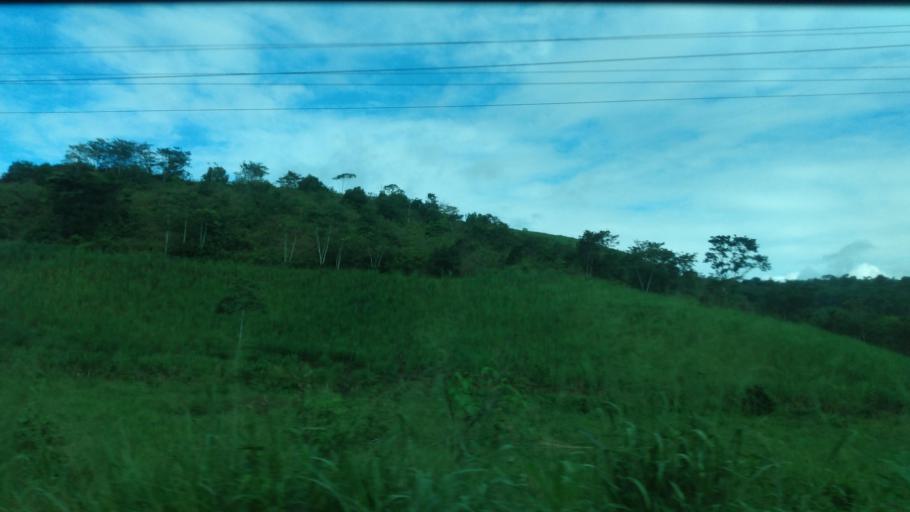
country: BR
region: Pernambuco
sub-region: Catende
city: Catende
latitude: -8.7045
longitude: -35.7486
